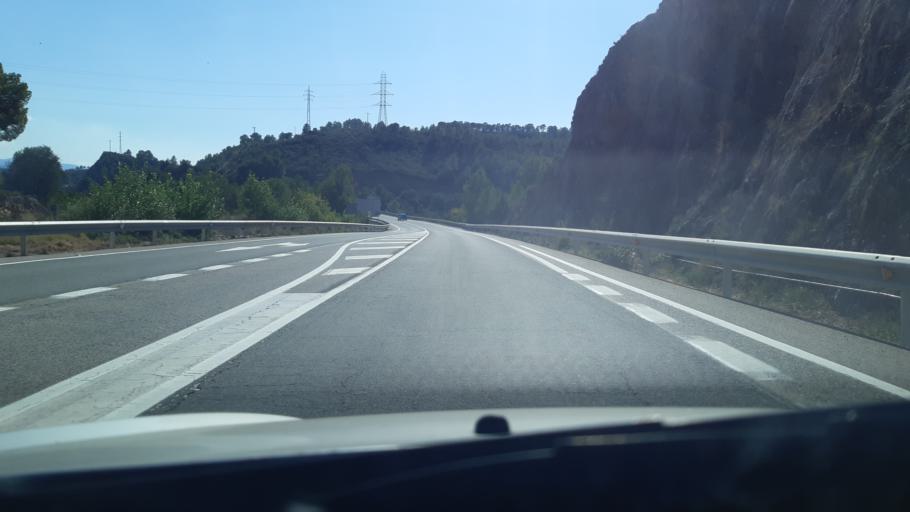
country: ES
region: Catalonia
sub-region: Provincia de Tarragona
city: Tivenys
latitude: 40.9318
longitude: 0.4848
